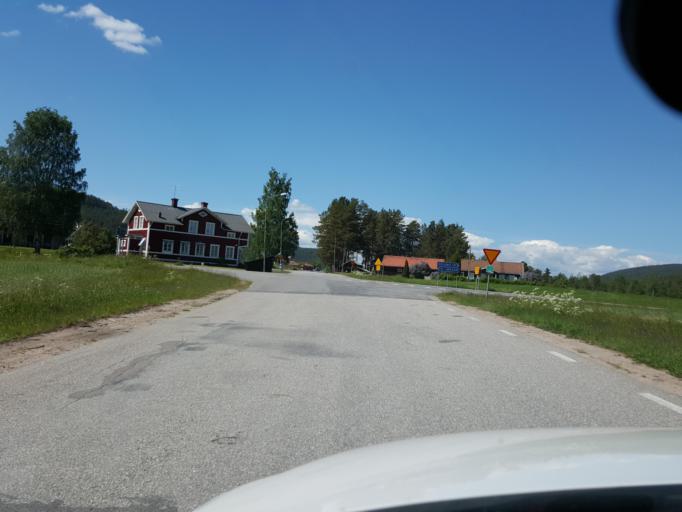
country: SE
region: Gaevleborg
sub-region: Ljusdals Kommun
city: Jaervsoe
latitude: 61.7117
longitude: 16.3000
